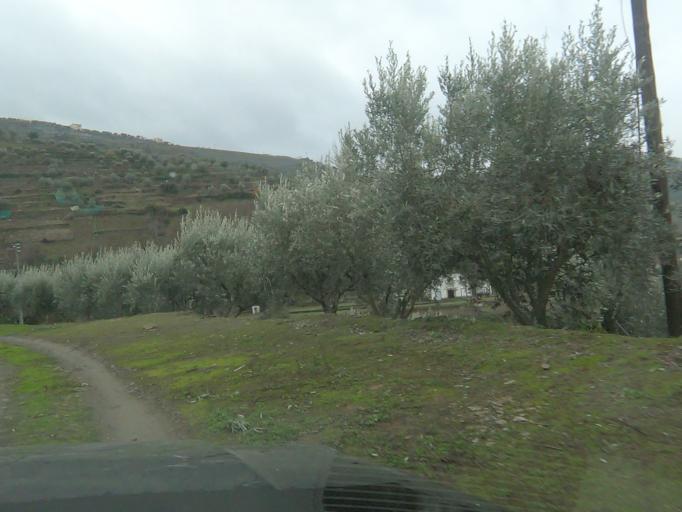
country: PT
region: Vila Real
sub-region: Vila Real
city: Vila Real
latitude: 41.2393
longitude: -7.7391
